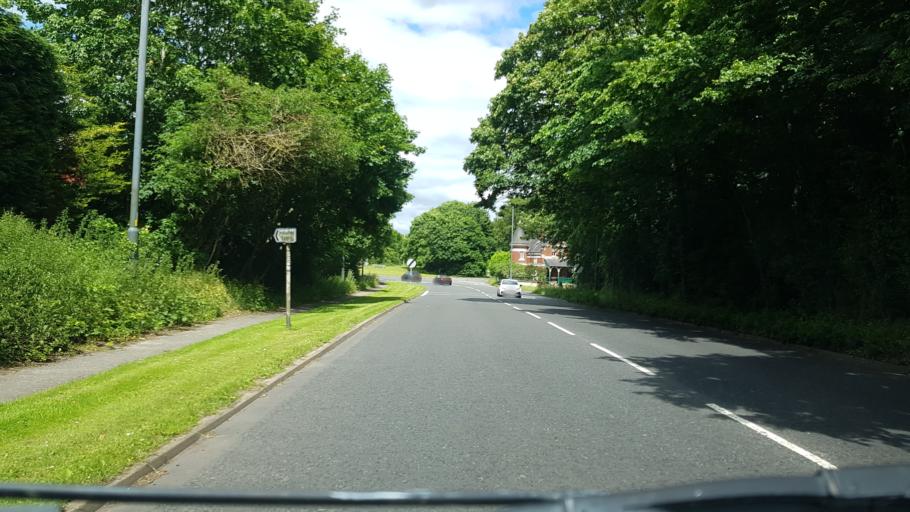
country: GB
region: England
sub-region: Worcestershire
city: Droitwich
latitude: 52.2724
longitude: -2.1409
